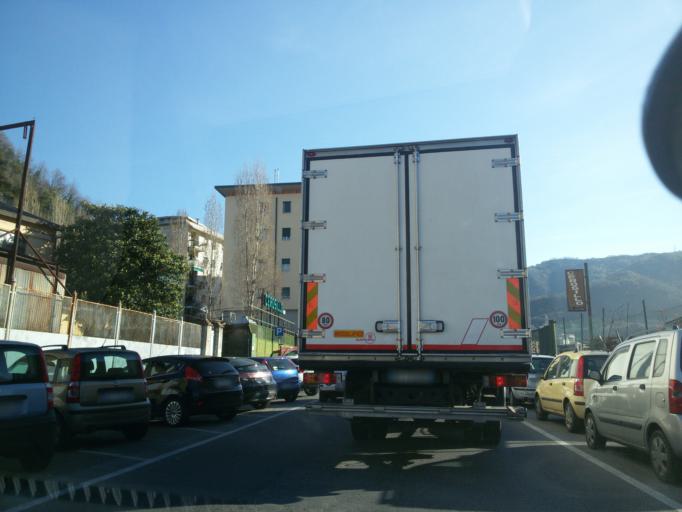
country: IT
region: Liguria
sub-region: Provincia di Genova
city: Piccarello
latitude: 44.4502
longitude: 8.9733
